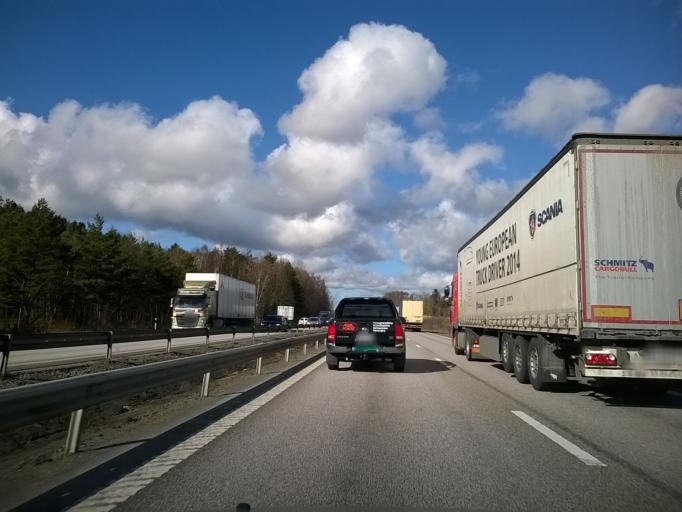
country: SE
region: Vaestra Goetaland
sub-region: Molndal
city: Lindome
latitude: 57.5830
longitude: 12.0631
